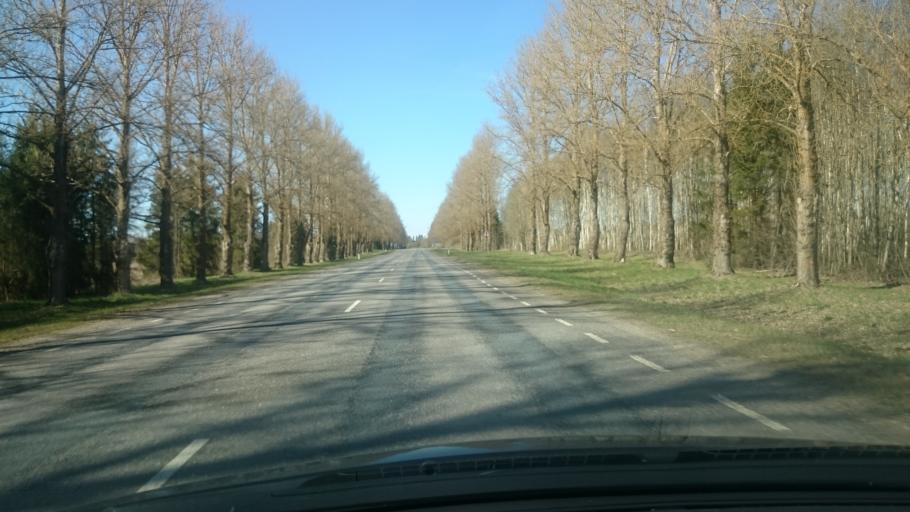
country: EE
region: Polvamaa
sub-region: Polva linn
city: Polva
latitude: 58.2961
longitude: 27.0015
